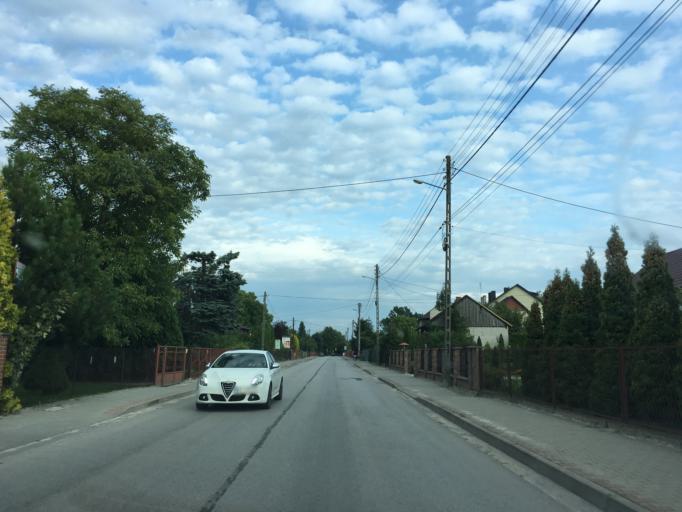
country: PL
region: Swietokrzyskie
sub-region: Powiat wloszczowski
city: Wloszczowa
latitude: 50.8484
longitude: 19.9866
